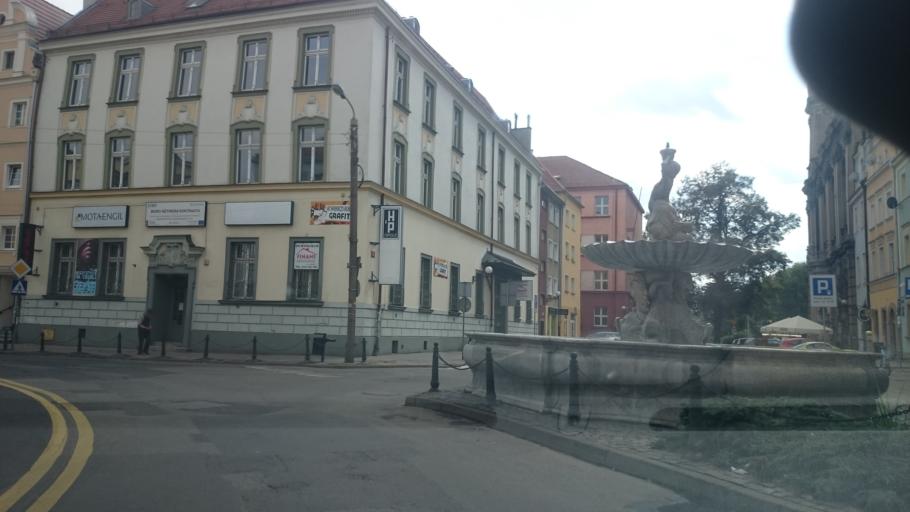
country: PL
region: Opole Voivodeship
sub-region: Powiat nyski
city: Nysa
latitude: 50.4725
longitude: 17.3327
